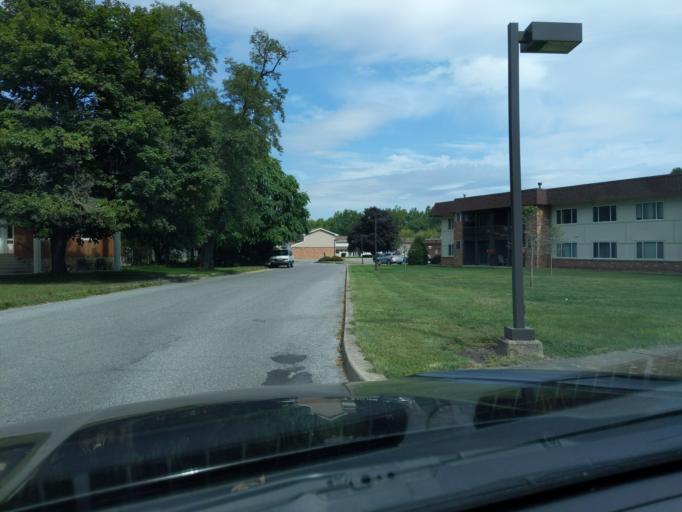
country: US
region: Pennsylvania
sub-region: Blair County
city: Duncansville
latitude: 40.4261
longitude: -78.4276
